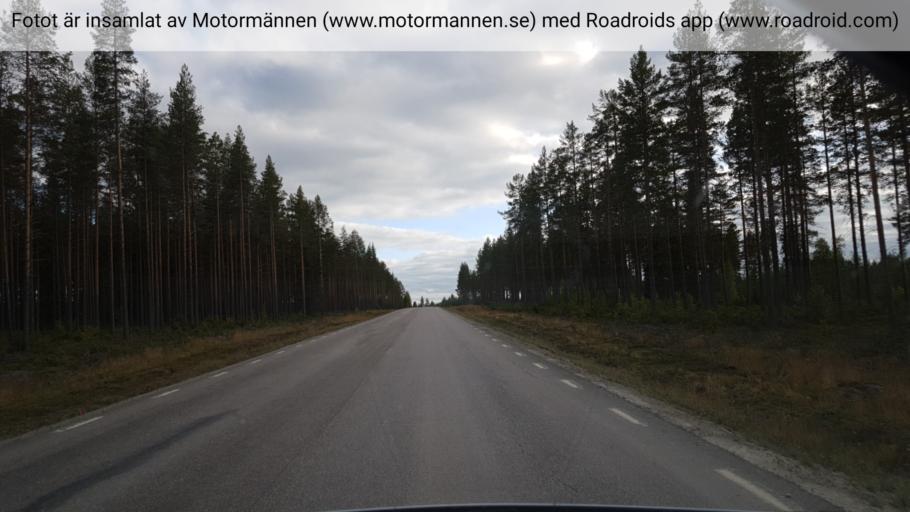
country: SE
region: Vaesterbotten
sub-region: Vindelns Kommun
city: Vindeln
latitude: 64.0780
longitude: 19.6335
